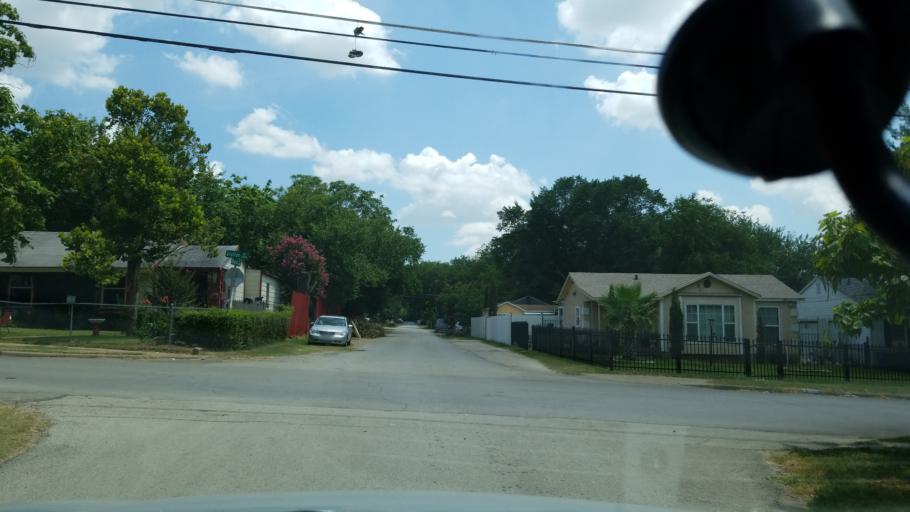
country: US
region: Texas
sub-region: Dallas County
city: Cockrell Hill
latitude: 32.7303
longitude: -96.8769
